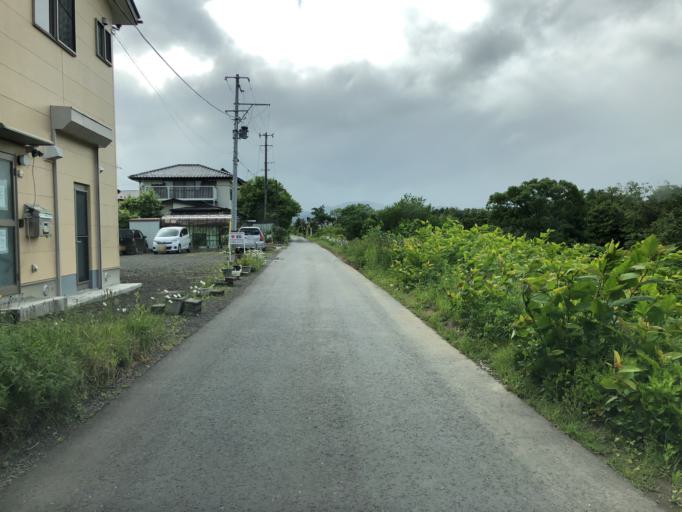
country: JP
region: Fukushima
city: Fukushima-shi
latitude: 37.7811
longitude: 140.4791
